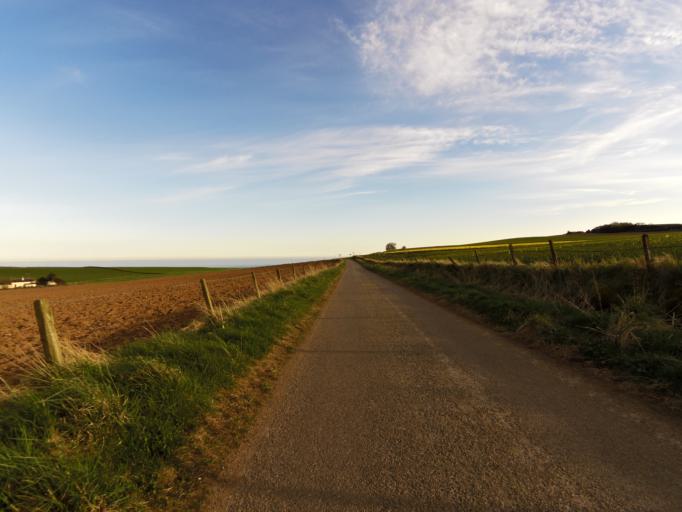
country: GB
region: Scotland
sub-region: Aberdeenshire
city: Inverbervie
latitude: 56.8799
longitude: -2.2359
